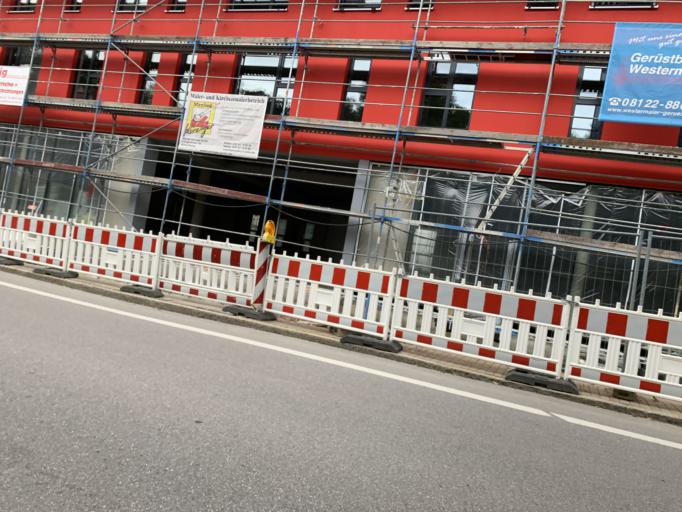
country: DE
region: Bavaria
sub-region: Upper Bavaria
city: Freising
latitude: 48.4082
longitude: 11.7446
